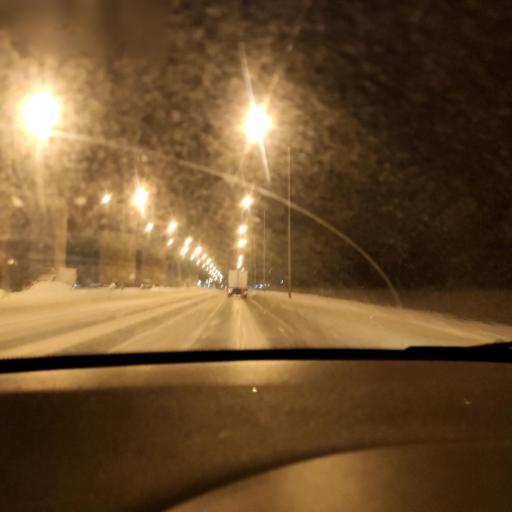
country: RU
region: Samara
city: Petra-Dubrava
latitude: 53.2971
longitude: 50.3321
